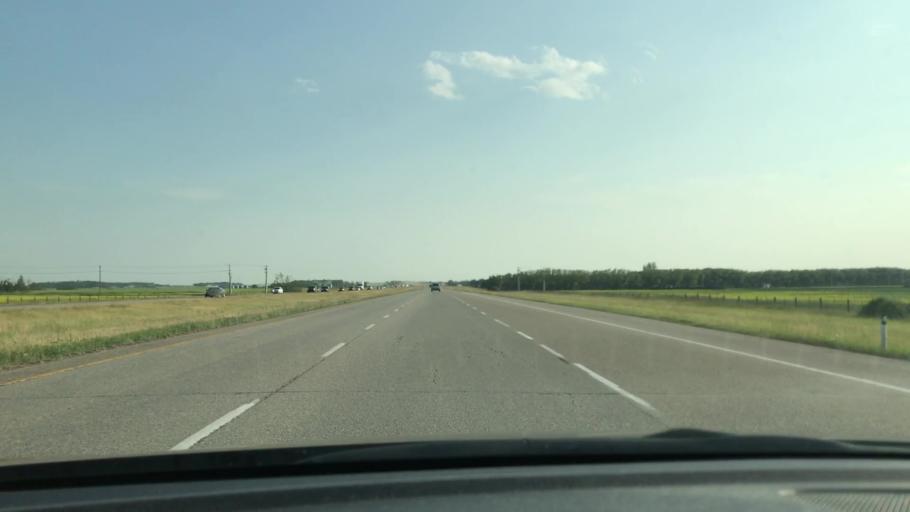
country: CA
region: Alberta
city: Leduc
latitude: 53.2250
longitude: -113.5771
